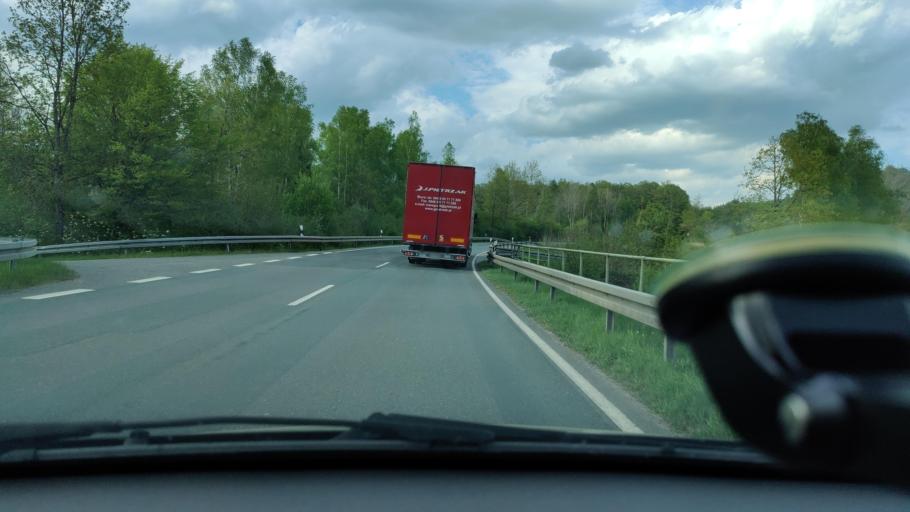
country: DE
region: North Rhine-Westphalia
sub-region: Regierungsbezirk Detmold
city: Wunnenberg
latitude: 51.4819
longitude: 8.6563
